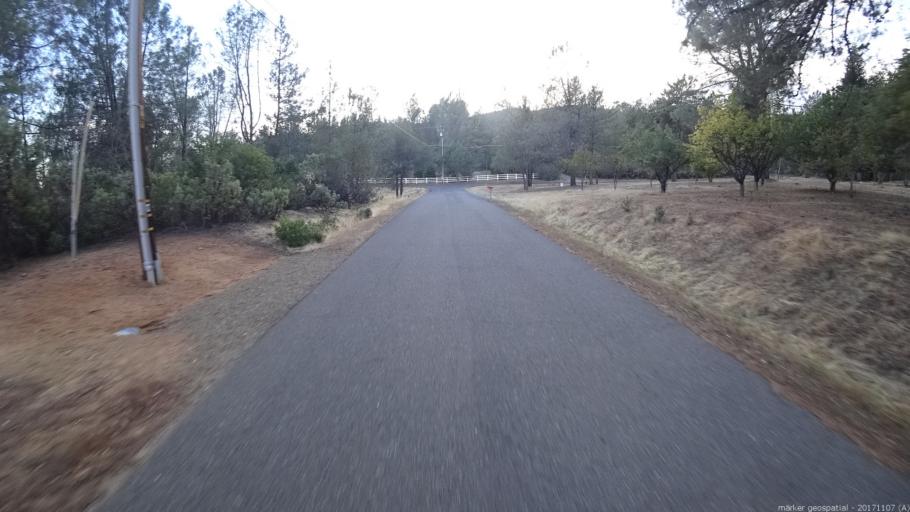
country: US
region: California
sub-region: Shasta County
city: Shasta
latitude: 40.5445
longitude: -122.4879
